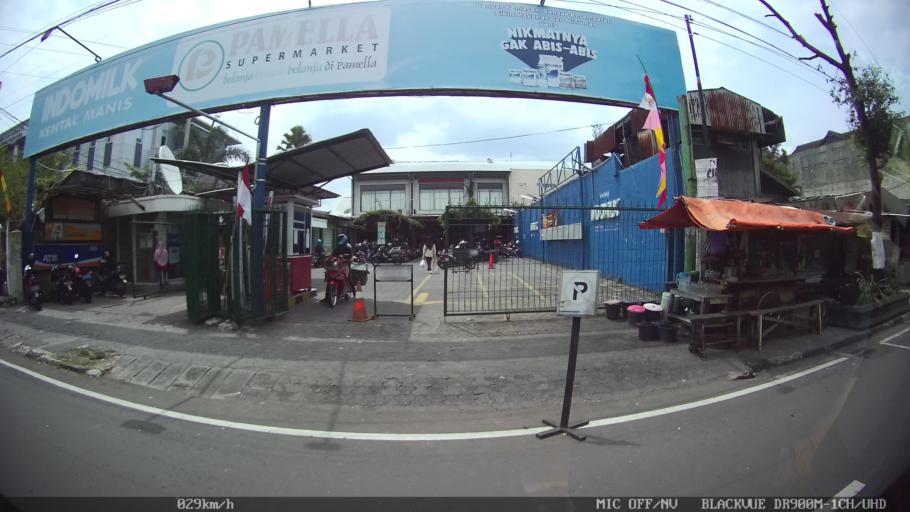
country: ID
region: Daerah Istimewa Yogyakarta
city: Yogyakarta
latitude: -7.8020
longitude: 110.3911
